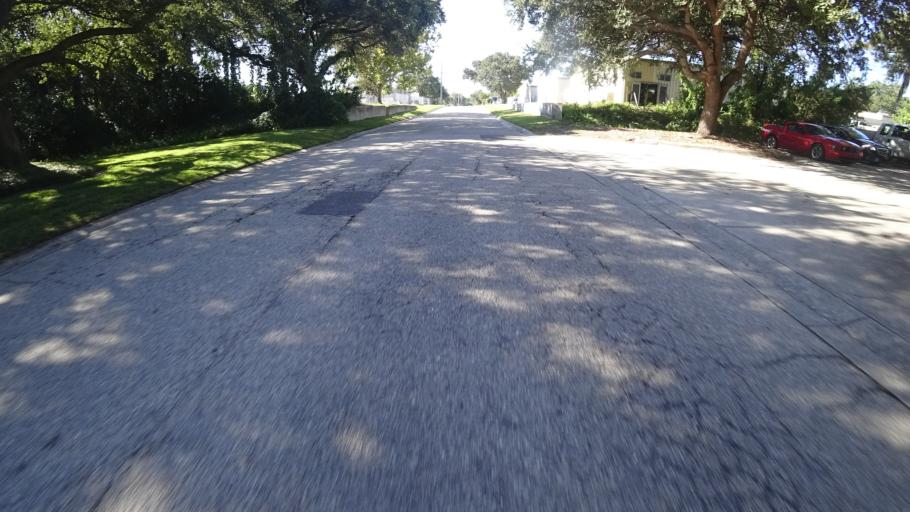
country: US
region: Florida
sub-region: Manatee County
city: Whitfield
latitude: 27.4240
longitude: -82.5342
